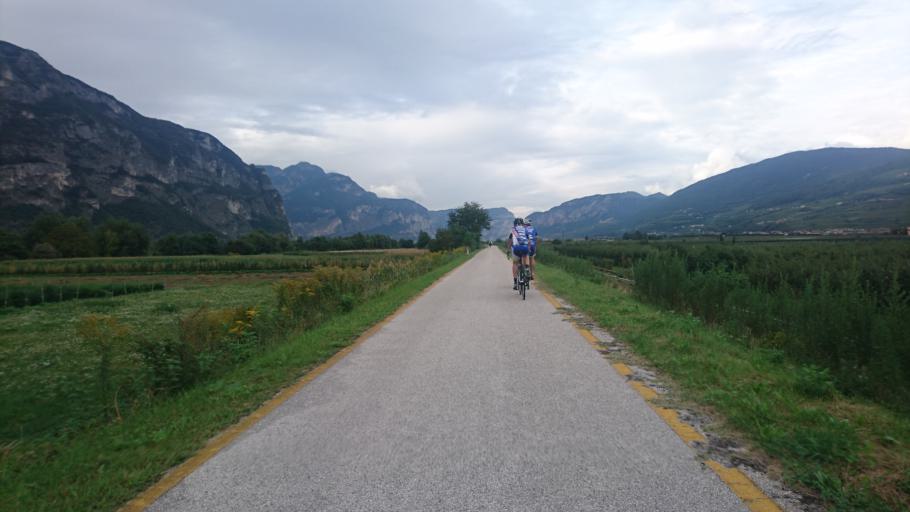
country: IT
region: Trentino-Alto Adige
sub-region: Provincia di Trento
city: Zambana
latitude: 46.1484
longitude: 11.0803
